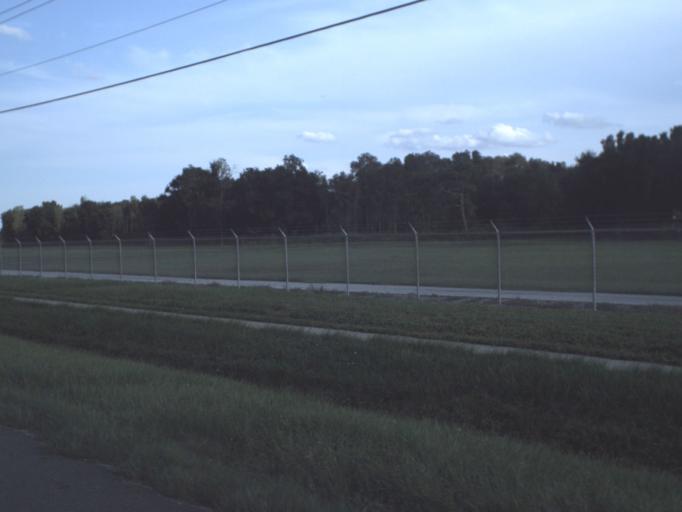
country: US
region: Florida
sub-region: Hillsborough County
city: Egypt Lake-Leto
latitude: 27.9961
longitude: -82.5327
